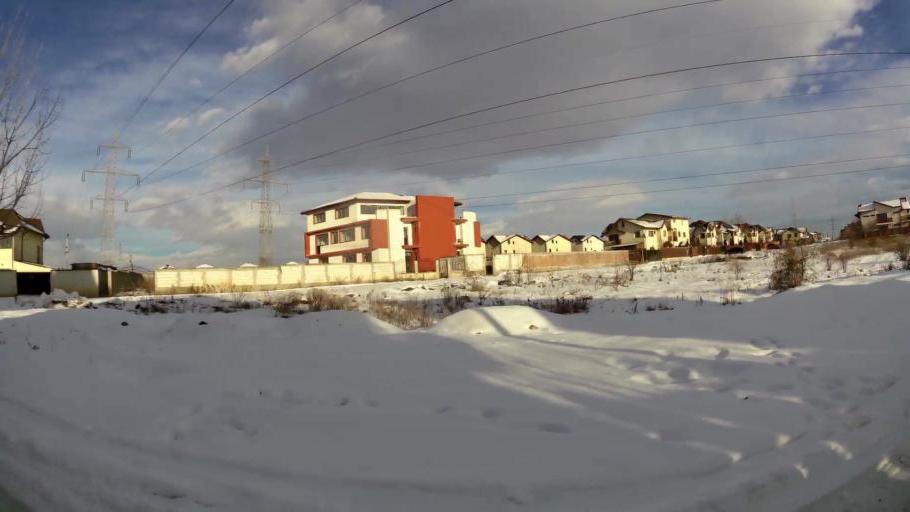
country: RO
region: Ilfov
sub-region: Comuna Fundeni-Dobroesti
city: Fundeni
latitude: 44.4642
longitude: 26.1738
